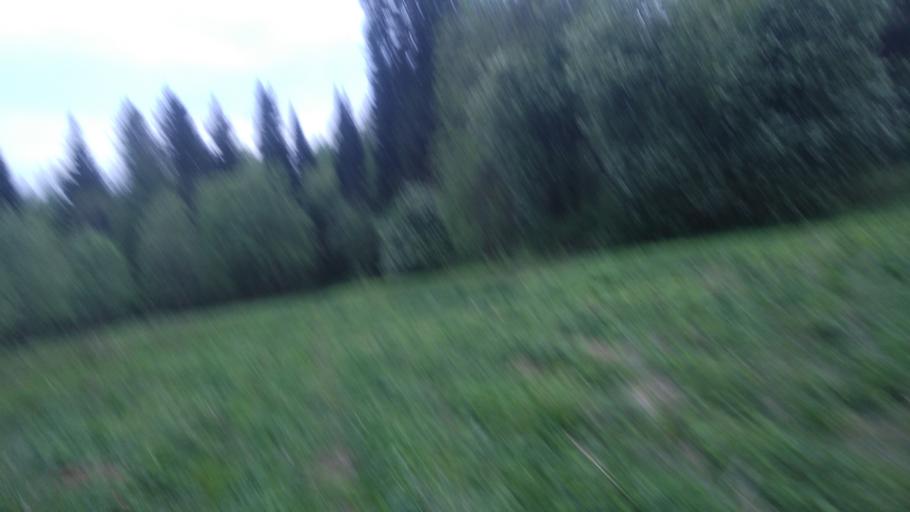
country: RU
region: Perm
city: Froly
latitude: 57.9643
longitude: 56.2995
